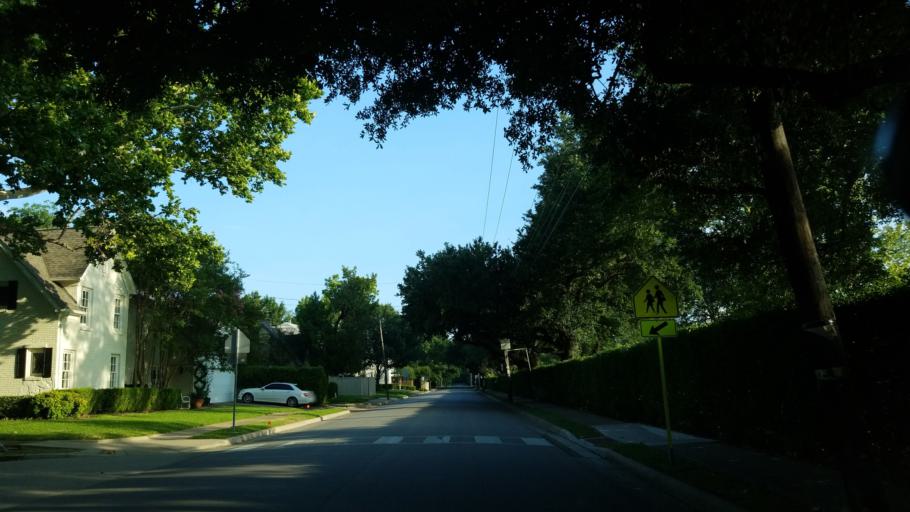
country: US
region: Texas
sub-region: Dallas County
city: University Park
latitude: 32.8422
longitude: -96.7956
